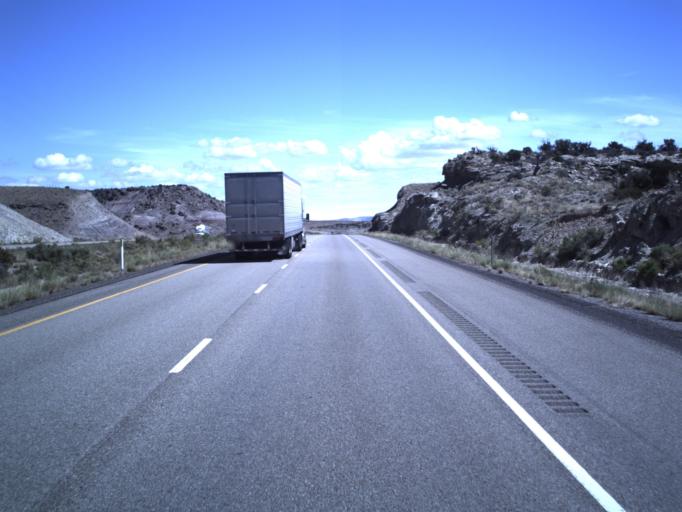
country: US
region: Utah
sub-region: Emery County
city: Ferron
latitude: 38.8169
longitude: -111.1745
